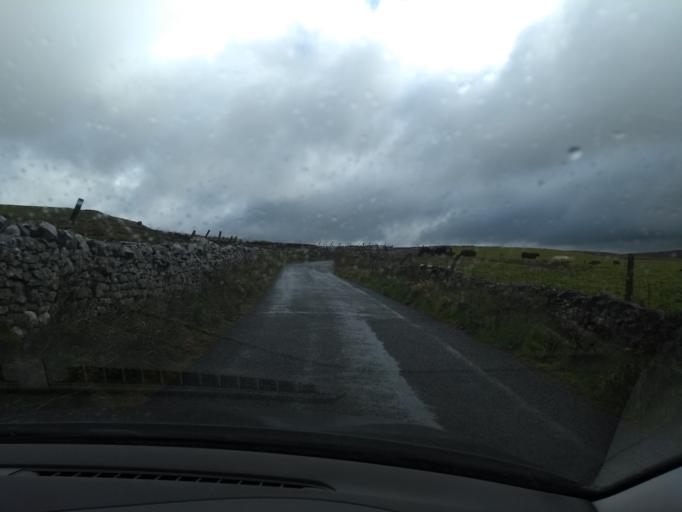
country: GB
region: England
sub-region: North Yorkshire
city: Settle
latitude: 54.0995
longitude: -2.2132
